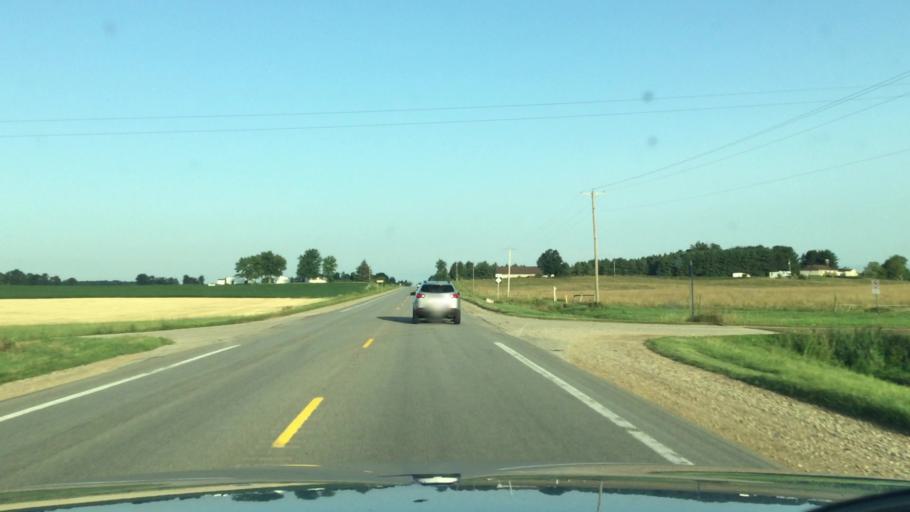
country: US
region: Michigan
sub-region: Gratiot County
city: Ithaca
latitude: 43.1760
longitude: -84.6193
